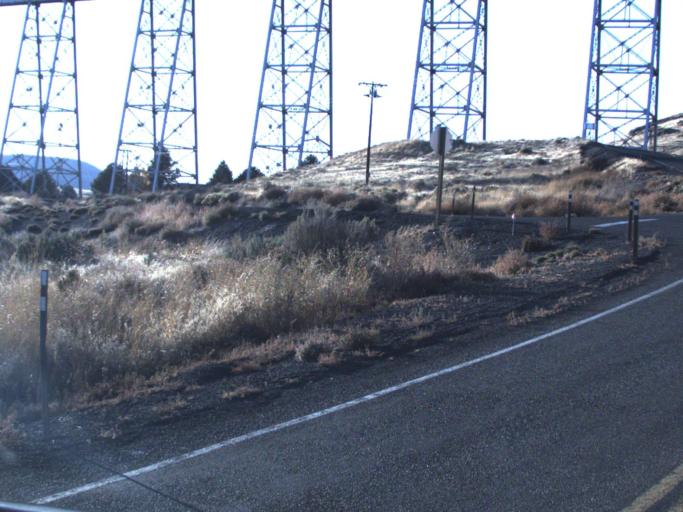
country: US
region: Washington
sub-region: Walla Walla County
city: Waitsburg
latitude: 46.5978
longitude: -118.2214
